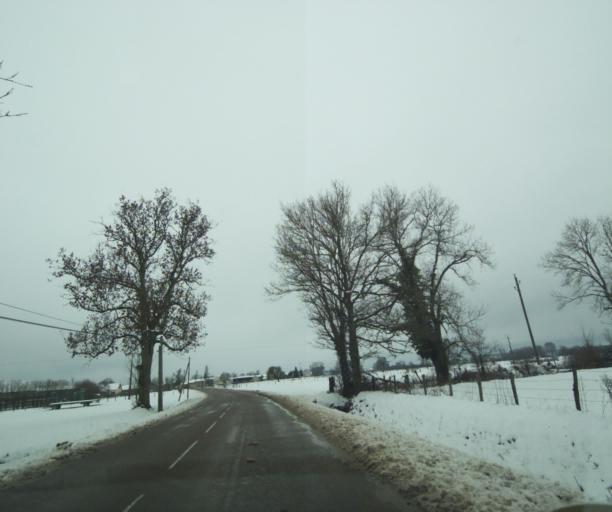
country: FR
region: Champagne-Ardenne
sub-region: Departement de la Haute-Marne
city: Montier-en-Der
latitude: 48.4549
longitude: 4.7724
